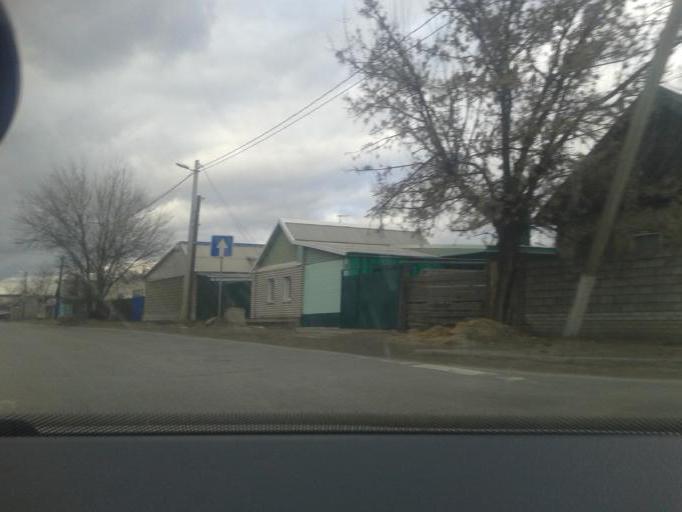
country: RU
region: Volgograd
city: Volgograd
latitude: 48.6993
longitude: 44.4737
